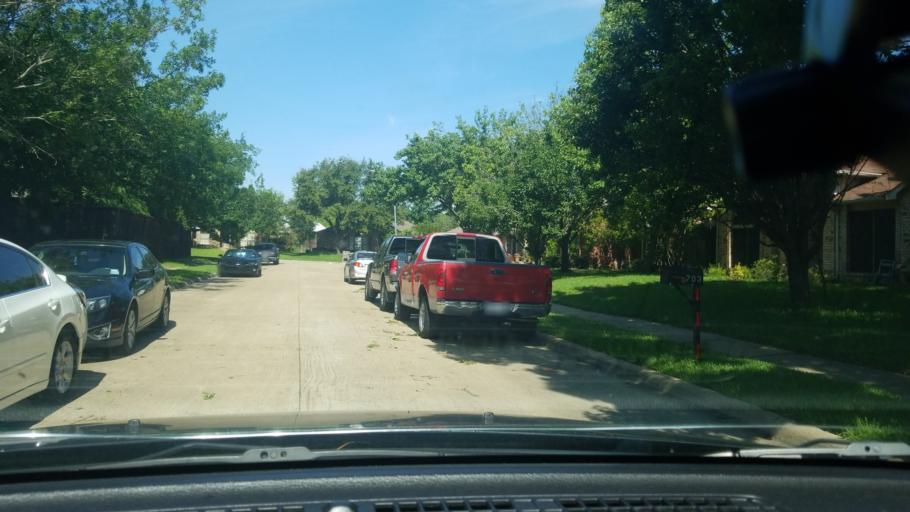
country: US
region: Texas
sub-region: Dallas County
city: Mesquite
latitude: 32.7776
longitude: -96.5878
